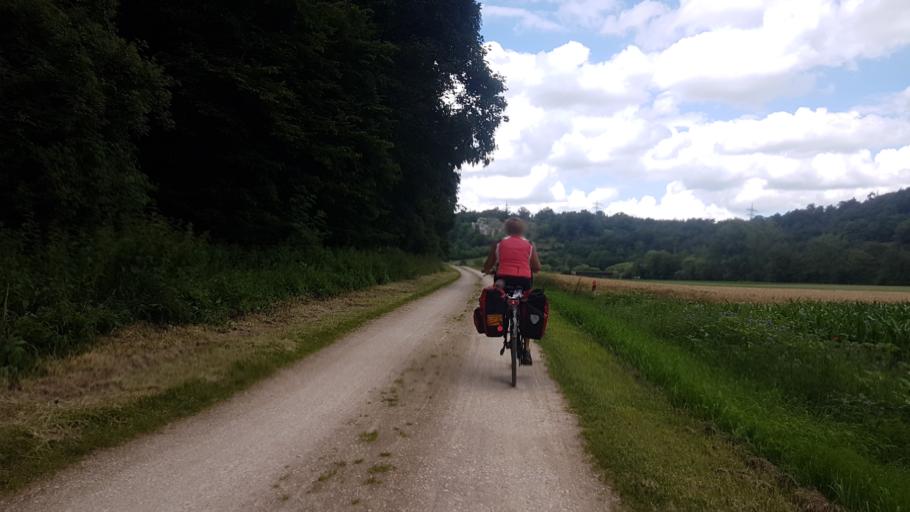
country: DE
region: Bavaria
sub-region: Regierungsbezirk Mittelfranken
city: Solnhofen
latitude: 48.8817
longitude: 11.0316
